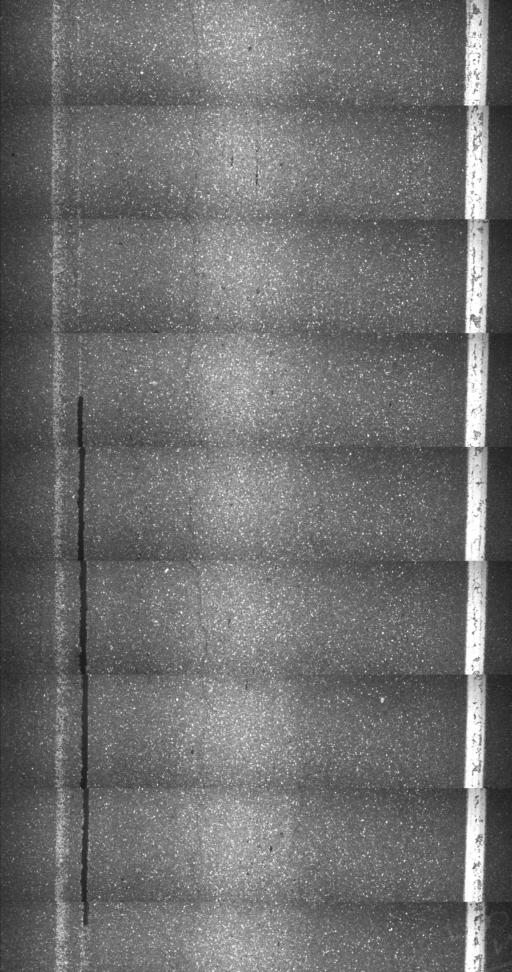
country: US
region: Vermont
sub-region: Windsor County
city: Windsor
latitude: 43.5471
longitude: -72.4145
